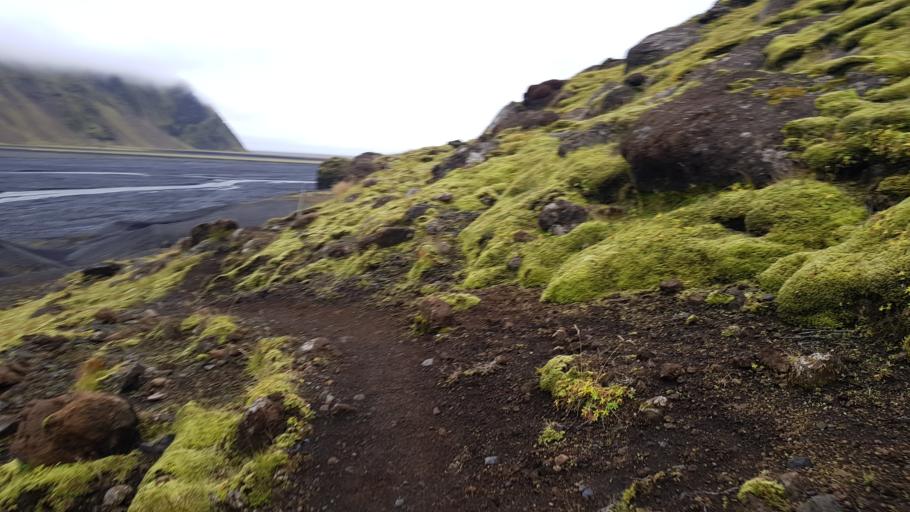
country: IS
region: South
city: Vestmannaeyjar
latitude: 63.5300
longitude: -18.8490
